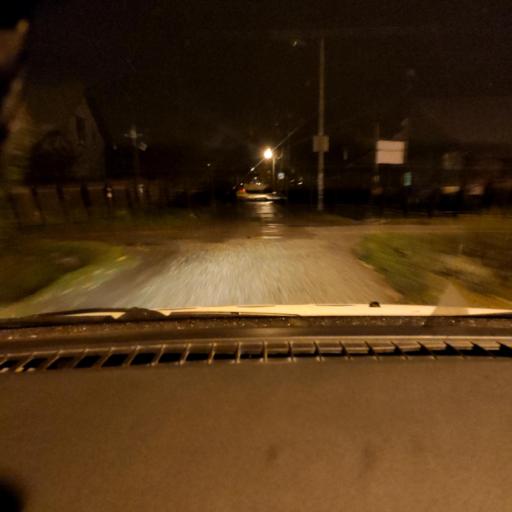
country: RU
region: Perm
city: Kondratovo
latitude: 58.0279
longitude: 55.9963
